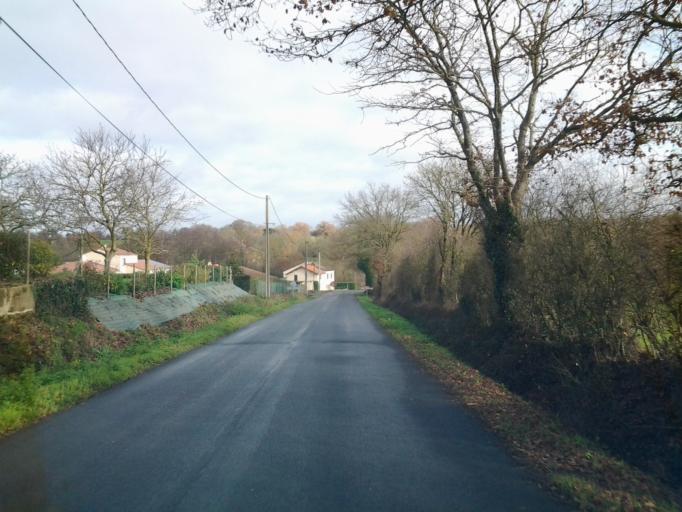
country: FR
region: Pays de la Loire
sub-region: Departement de la Vendee
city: Saint-Florent-des-Bois
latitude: 46.6295
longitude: -1.3101
